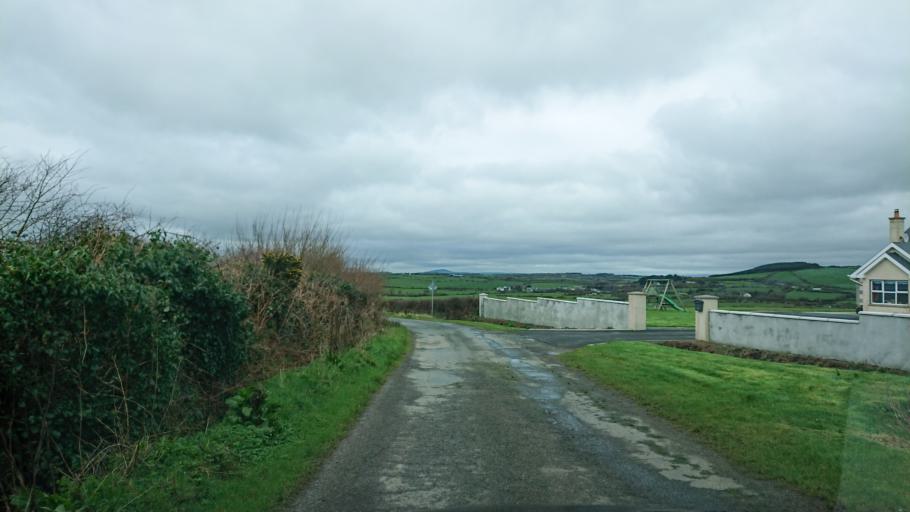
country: IE
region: Munster
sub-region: Waterford
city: Dunmore East
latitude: 52.1625
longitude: -7.0344
